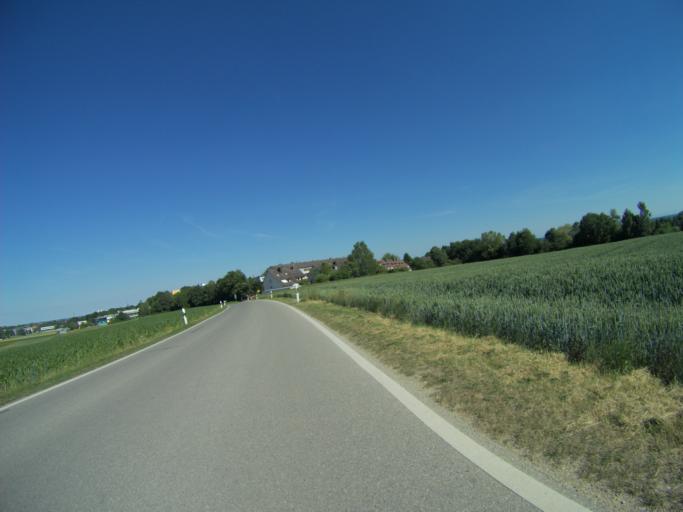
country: DE
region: Bavaria
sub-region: Upper Bavaria
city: Freising
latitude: 48.3983
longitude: 11.7059
